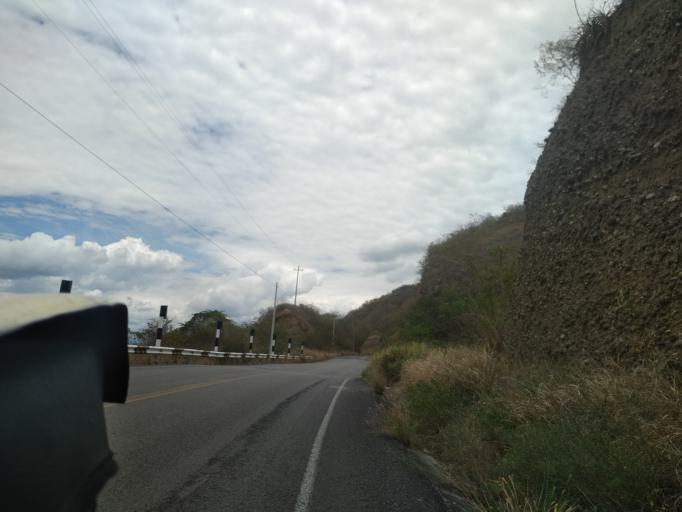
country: PE
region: Cajamarca
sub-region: Provincia de San Ignacio
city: La Coipa
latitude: -5.3901
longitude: -78.7777
